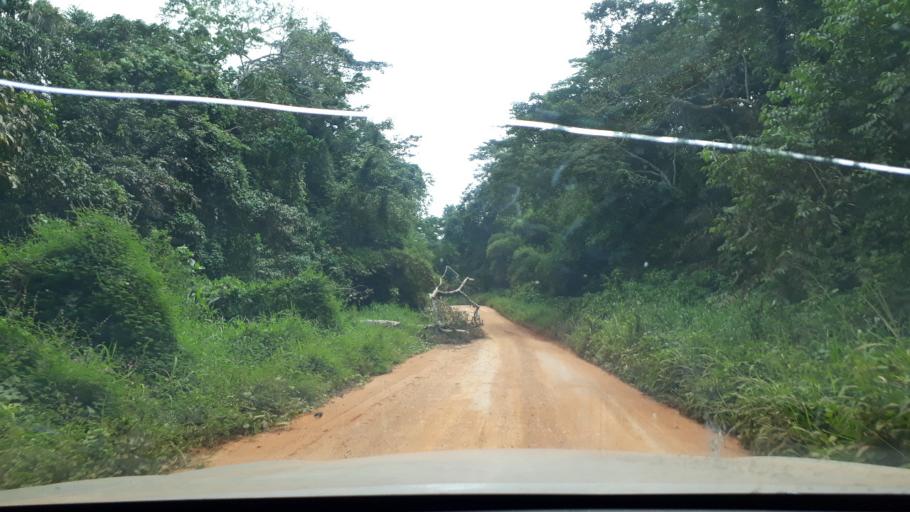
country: CD
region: Eastern Province
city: Wamba
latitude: 1.4057
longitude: 28.4213
